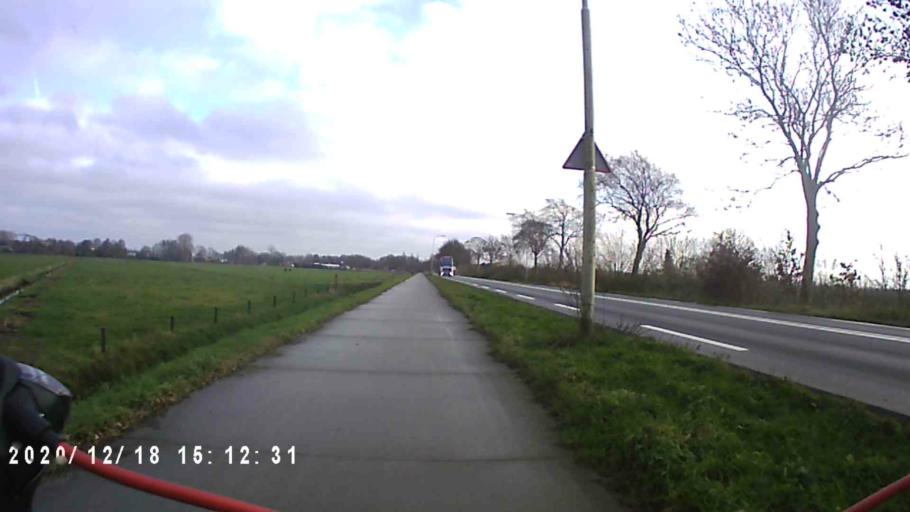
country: NL
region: Groningen
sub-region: Gemeente Hoogezand-Sappemeer
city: Hoogezand
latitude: 53.1647
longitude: 6.7131
